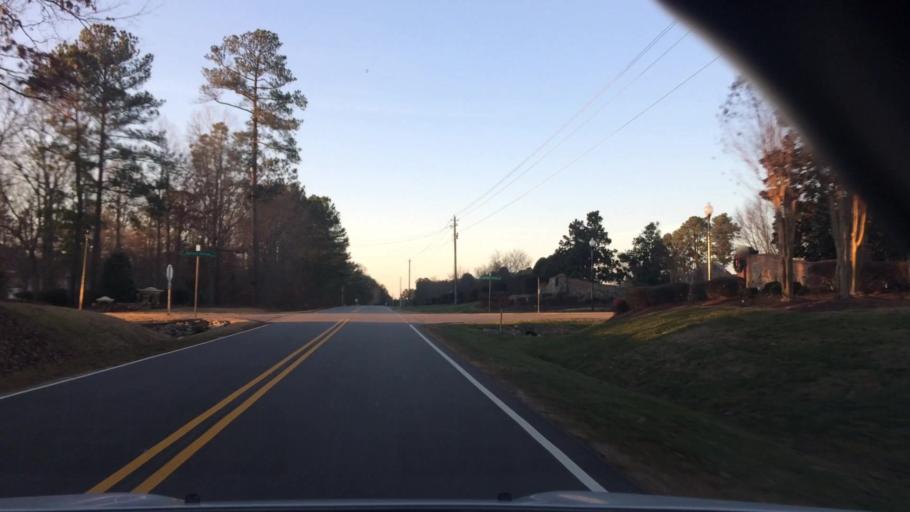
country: US
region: North Carolina
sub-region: Wake County
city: Rolesville
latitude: 35.9443
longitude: -78.4057
